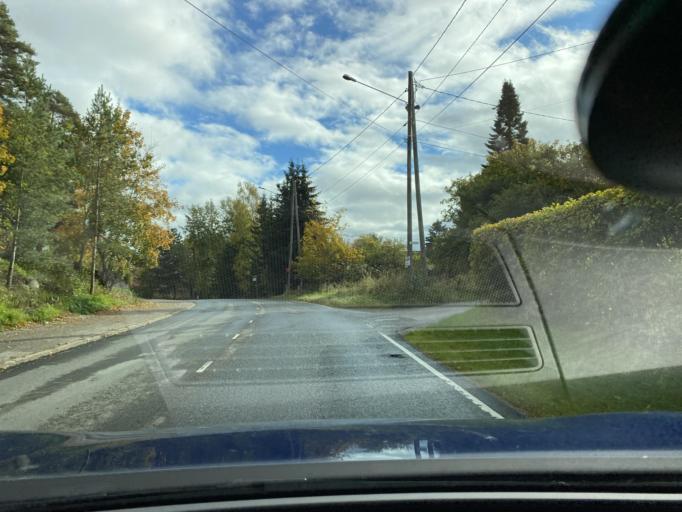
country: FI
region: Pirkanmaa
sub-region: Tampere
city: Nokia
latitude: 61.4772
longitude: 23.3401
